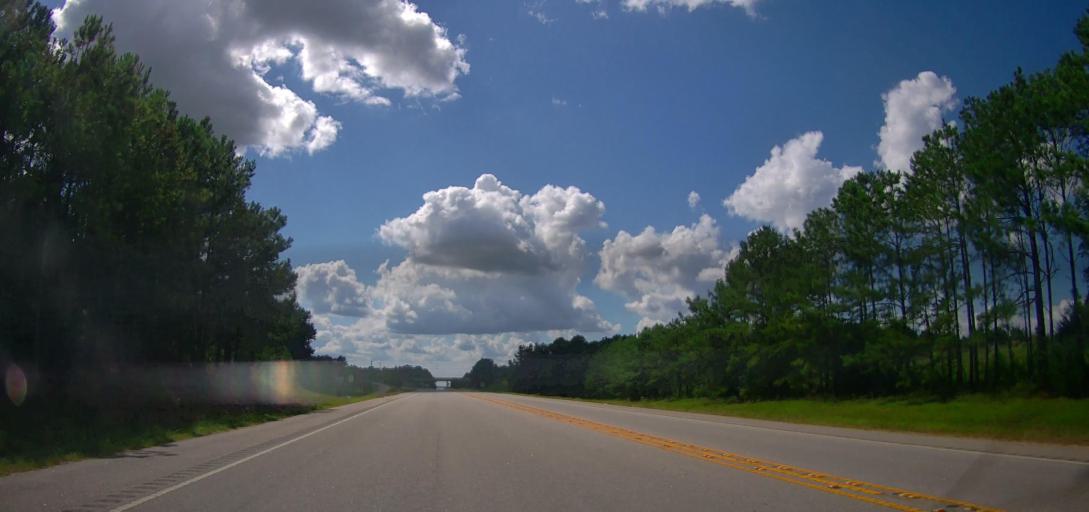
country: US
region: Alabama
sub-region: Macon County
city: Tuskegee
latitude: 32.4668
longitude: -85.5725
